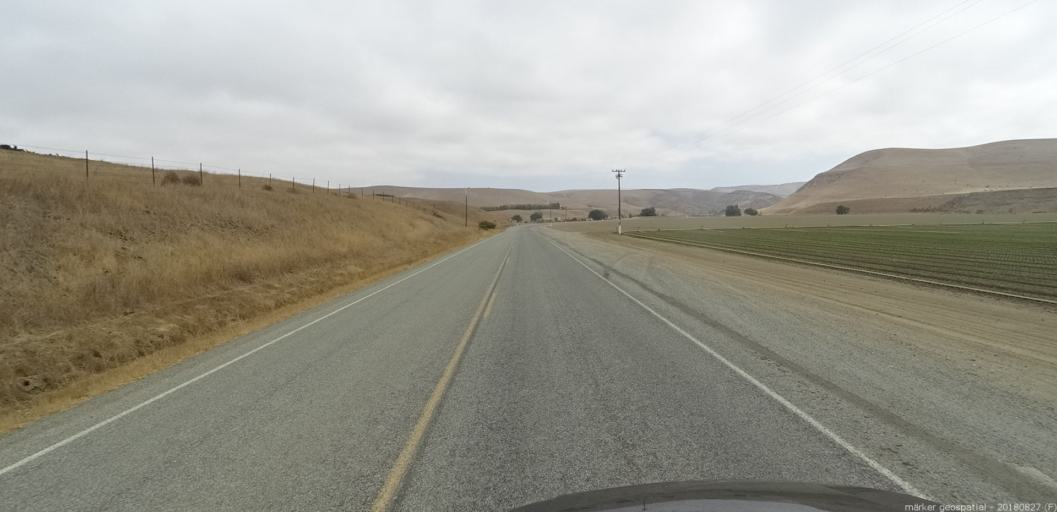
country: US
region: California
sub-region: Monterey County
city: King City
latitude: 36.2583
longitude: -121.0860
